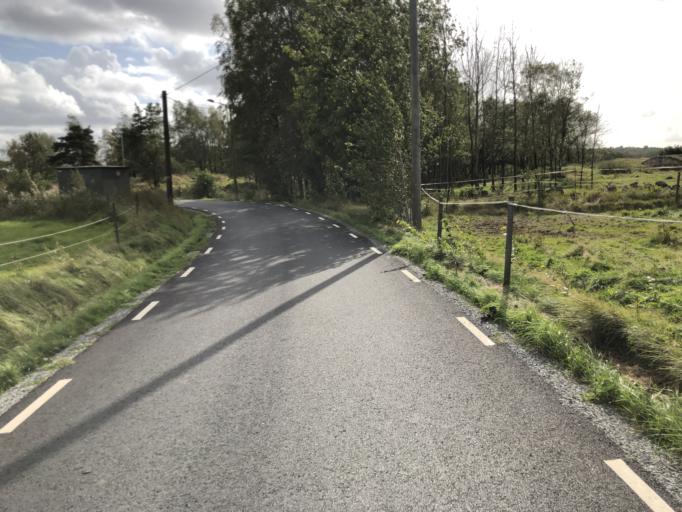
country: SE
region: Vaestra Goetaland
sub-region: Goteborg
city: Majorna
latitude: 57.7611
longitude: 11.8614
